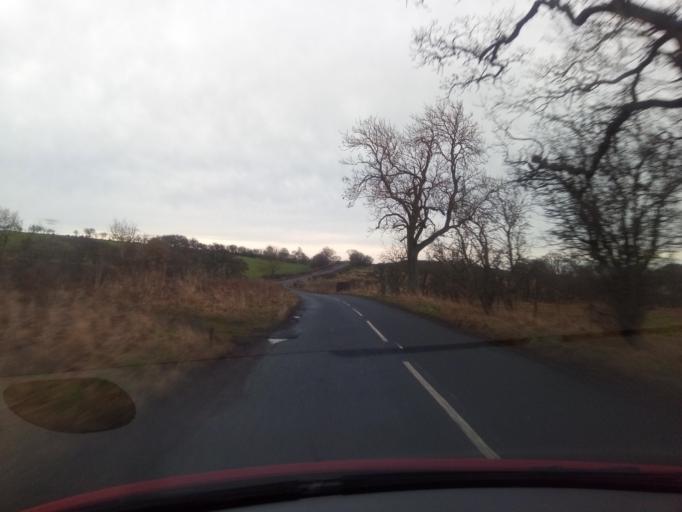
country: GB
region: England
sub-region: Northumberland
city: Ellingham
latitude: 55.4612
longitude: -1.8010
